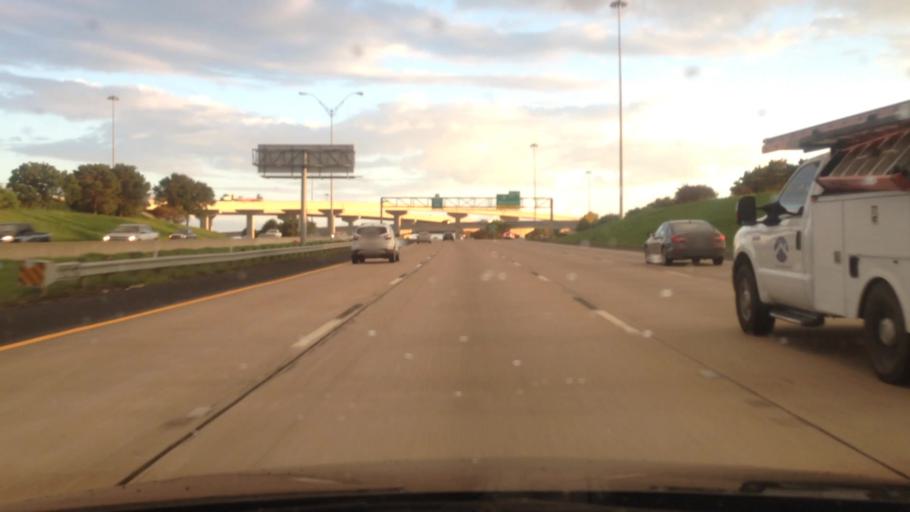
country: US
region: Texas
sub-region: Tarrant County
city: White Settlement
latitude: 32.7421
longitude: -97.4814
